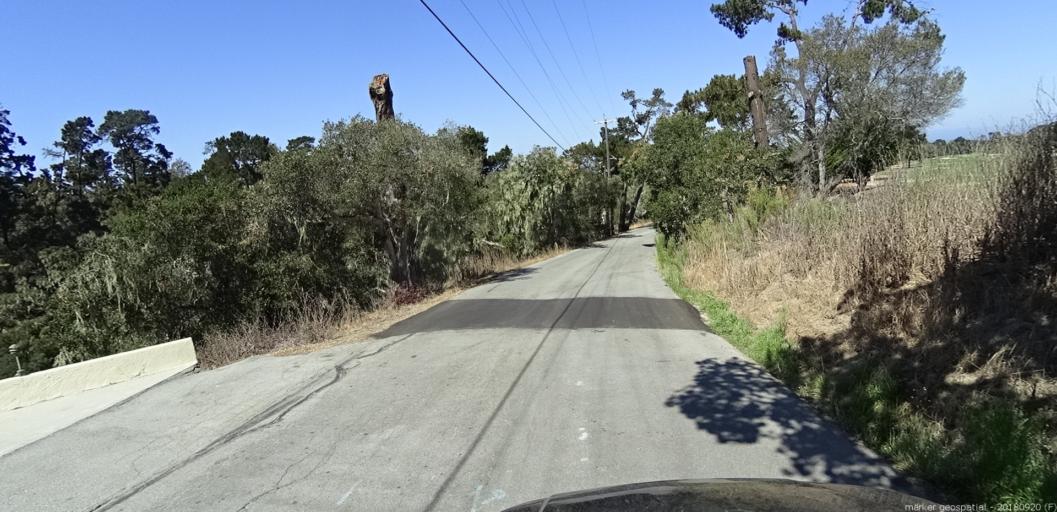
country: US
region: California
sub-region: Monterey County
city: Monterey
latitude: 36.5853
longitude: -121.8736
